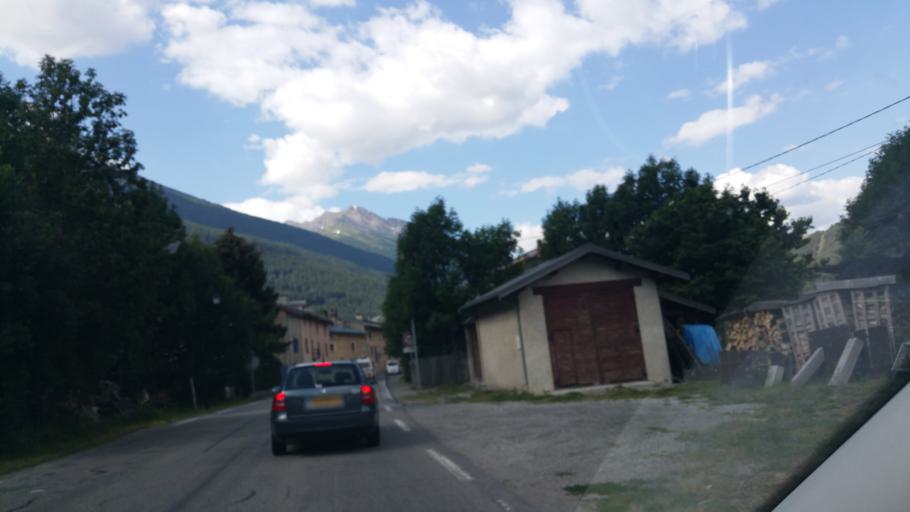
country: FR
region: Rhone-Alpes
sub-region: Departement de la Savoie
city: Modane
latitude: 45.2334
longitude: 6.7866
